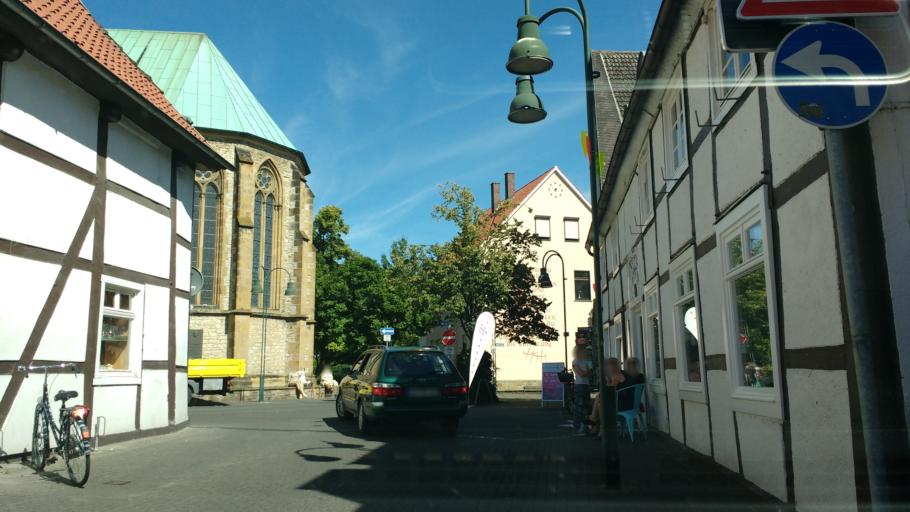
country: DE
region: North Rhine-Westphalia
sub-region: Regierungsbezirk Detmold
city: Rheda-Wiedenbruck
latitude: 51.8348
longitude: 8.3113
